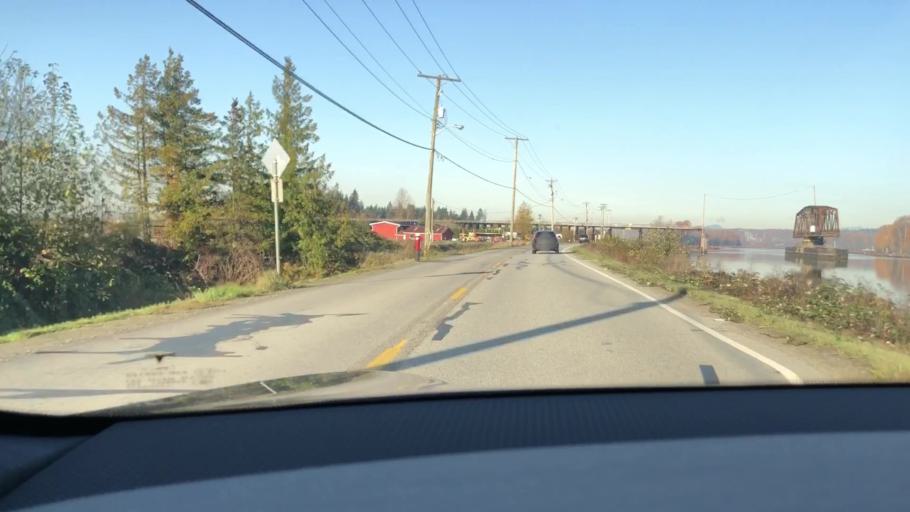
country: CA
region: British Columbia
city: New Westminster
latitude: 49.1805
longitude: -122.9844
